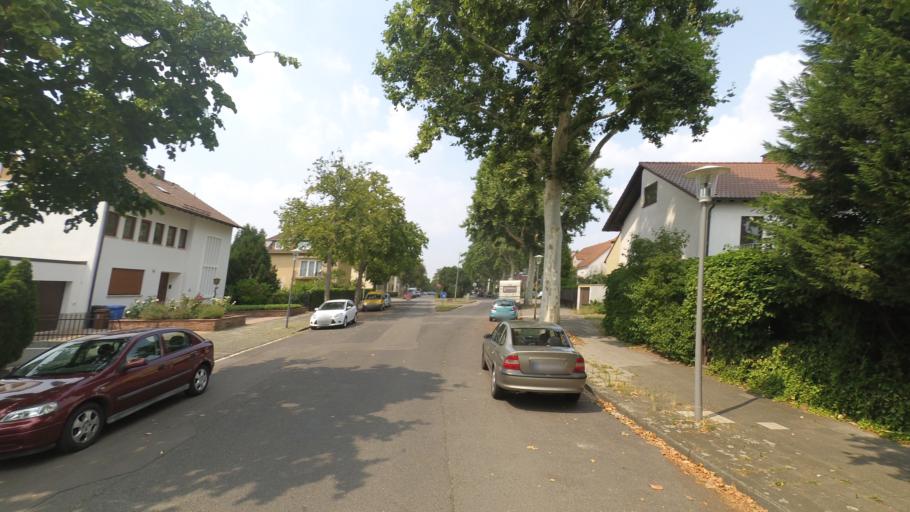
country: DE
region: Rheinland-Pfalz
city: Gartenstadt
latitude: 49.4589
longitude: 8.4121
